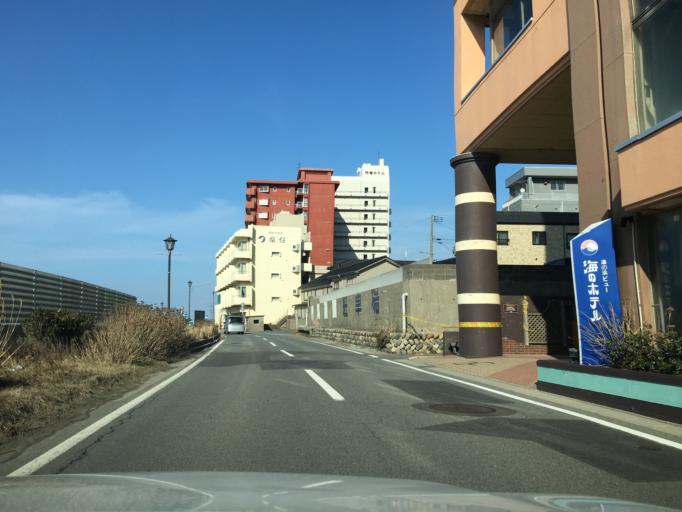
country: JP
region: Yamagata
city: Tsuruoka
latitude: 38.7795
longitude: 139.7508
